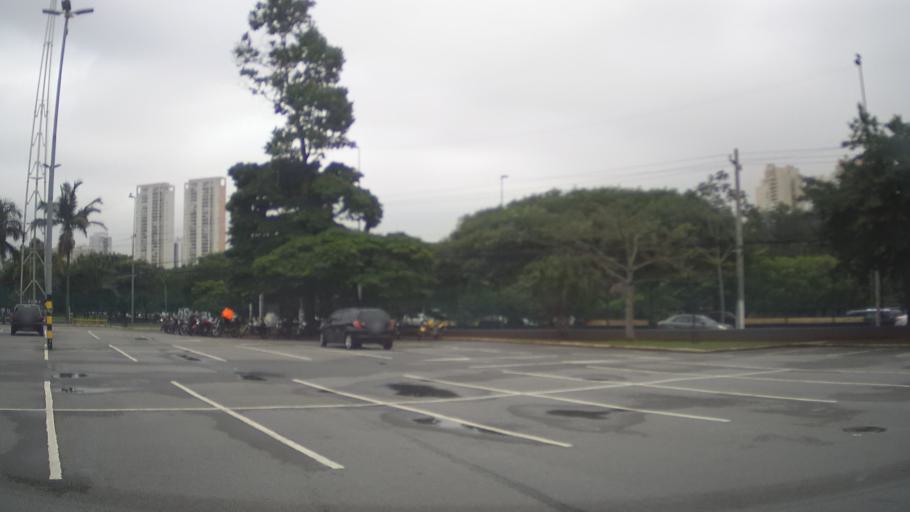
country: BR
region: Sao Paulo
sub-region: Sao Paulo
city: Sao Paulo
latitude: -23.5250
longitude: -46.5749
